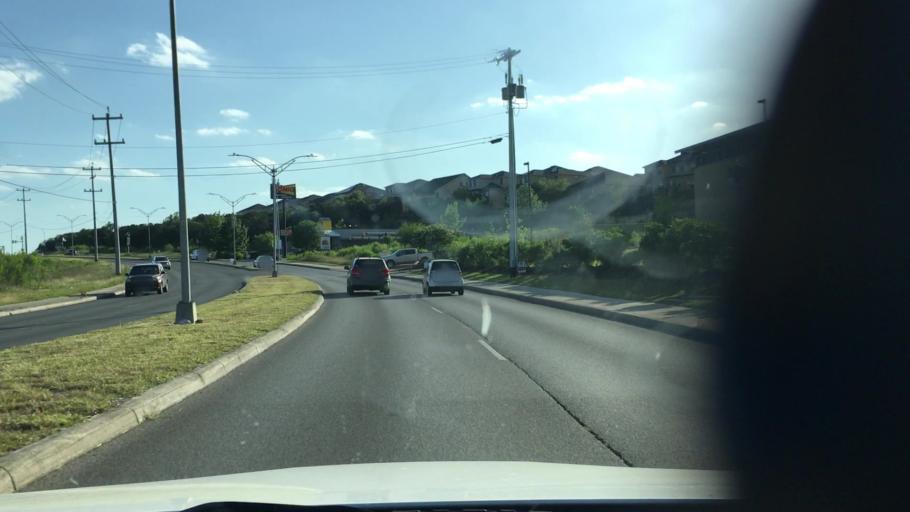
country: US
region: Texas
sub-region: Bexar County
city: Timberwood Park
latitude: 29.6604
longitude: -98.4365
